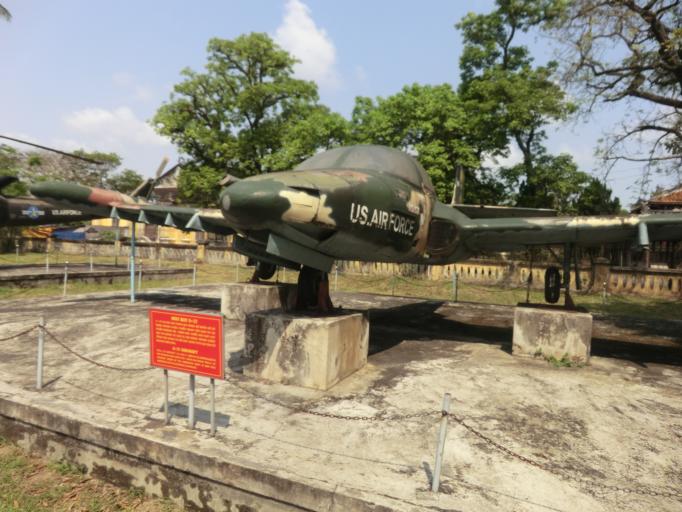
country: VN
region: Thua Thien-Hue
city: Hue
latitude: 16.4701
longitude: 107.5827
